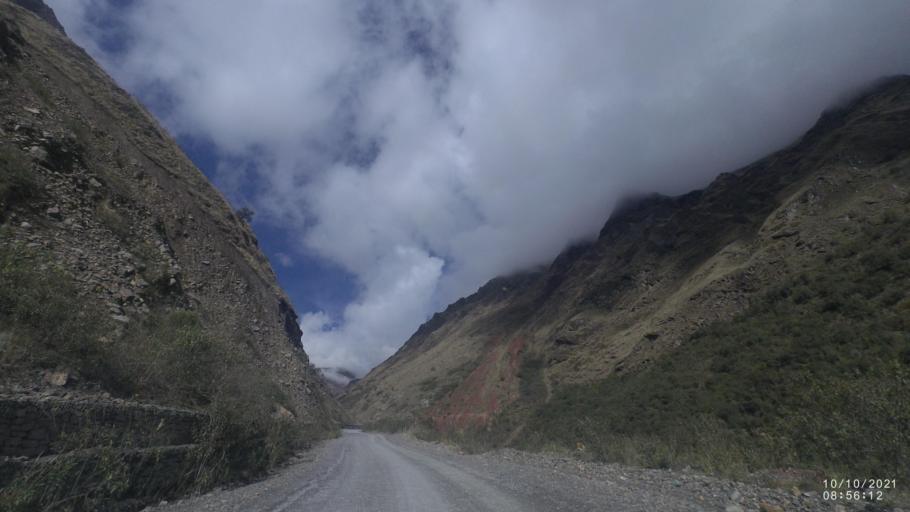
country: BO
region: La Paz
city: Quime
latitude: -16.9885
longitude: -67.2435
